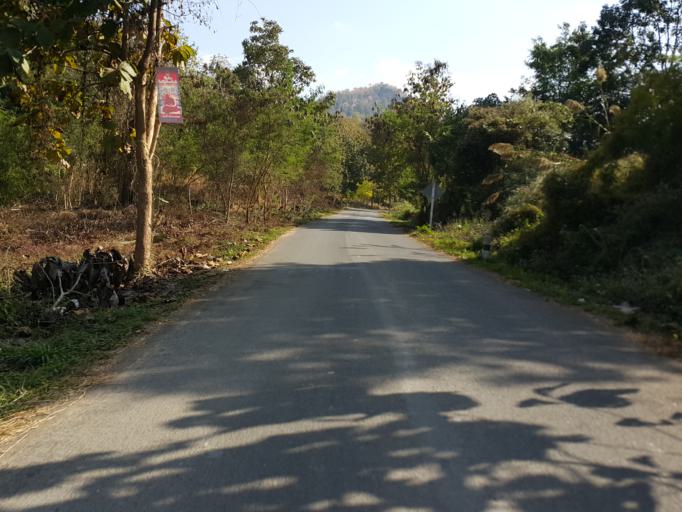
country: TH
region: Chiang Mai
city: Mae On
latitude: 18.7952
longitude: 99.2316
